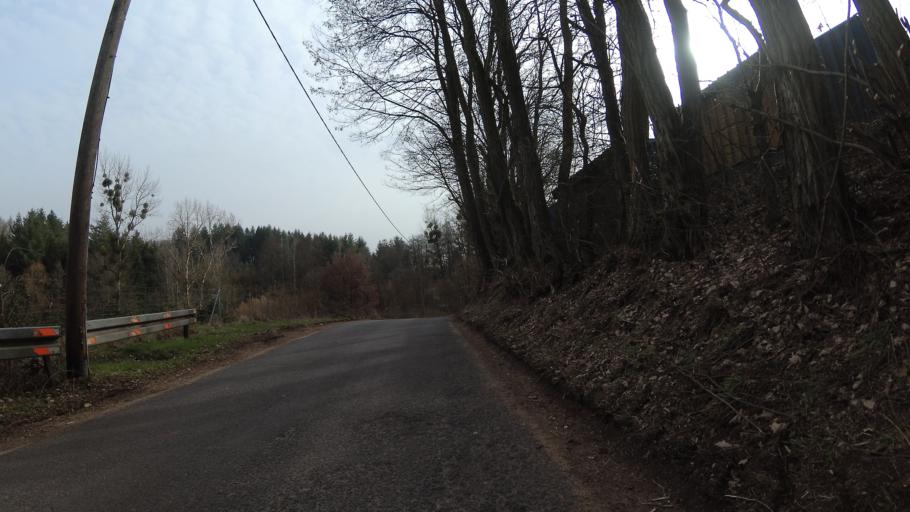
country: DE
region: Saarland
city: Nalbach
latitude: 49.4278
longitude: 6.7644
